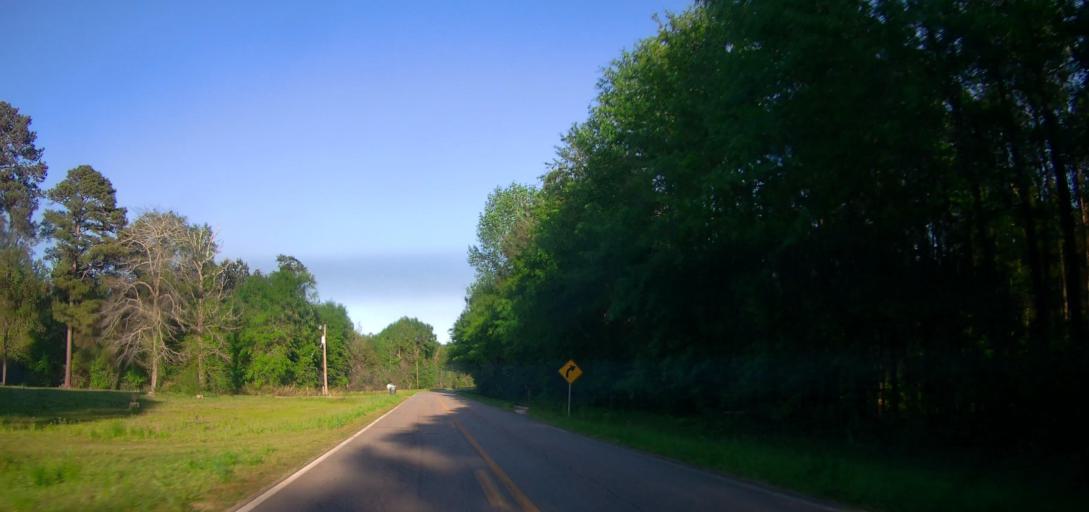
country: US
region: Georgia
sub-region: Macon County
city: Oglethorpe
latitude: 32.3049
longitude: -84.1084
